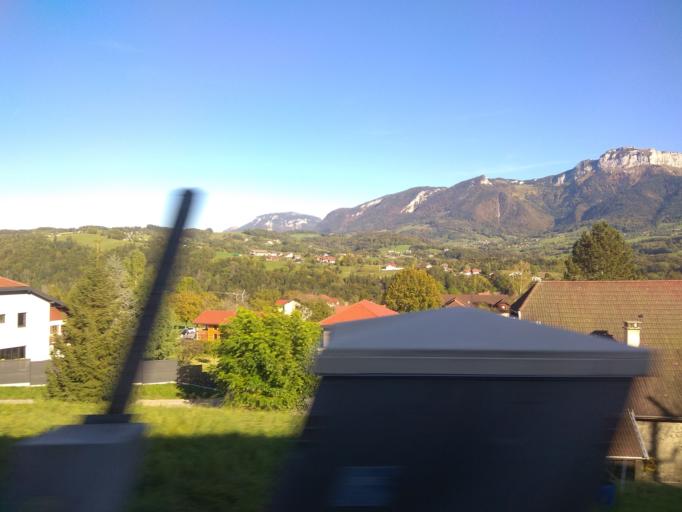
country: FR
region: Rhone-Alpes
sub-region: Departement de la Haute-Savoie
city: Saint-Martin-Bellevue
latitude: 45.9654
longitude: 6.1580
